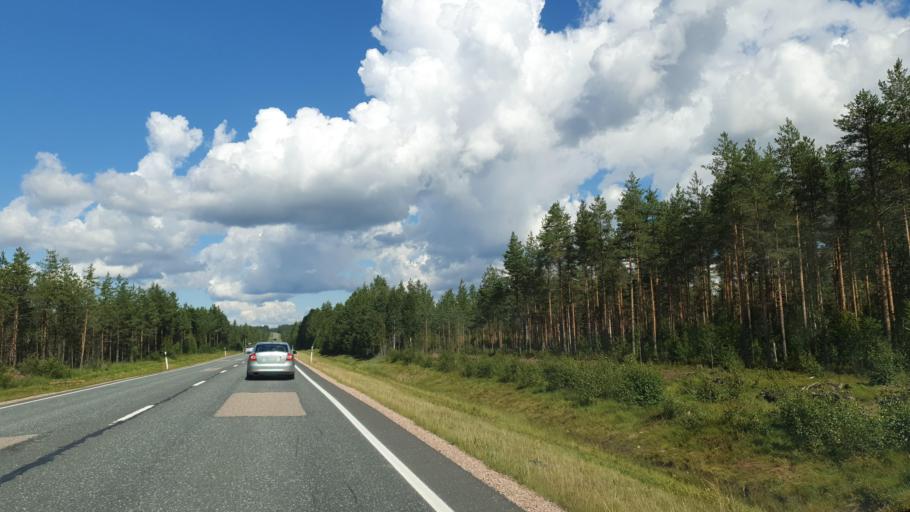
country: FI
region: Kainuu
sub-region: Kajaani
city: Kajaani
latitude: 64.0721
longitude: 27.4527
